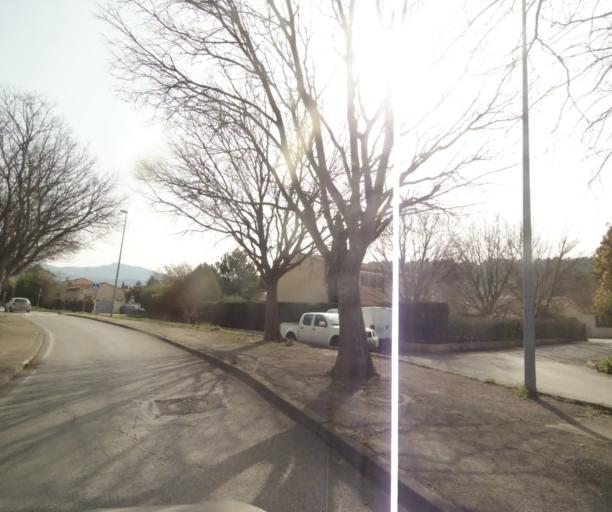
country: FR
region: Provence-Alpes-Cote d'Azur
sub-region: Departement des Bouches-du-Rhone
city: Gardanne
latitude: 43.4394
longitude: 5.4583
